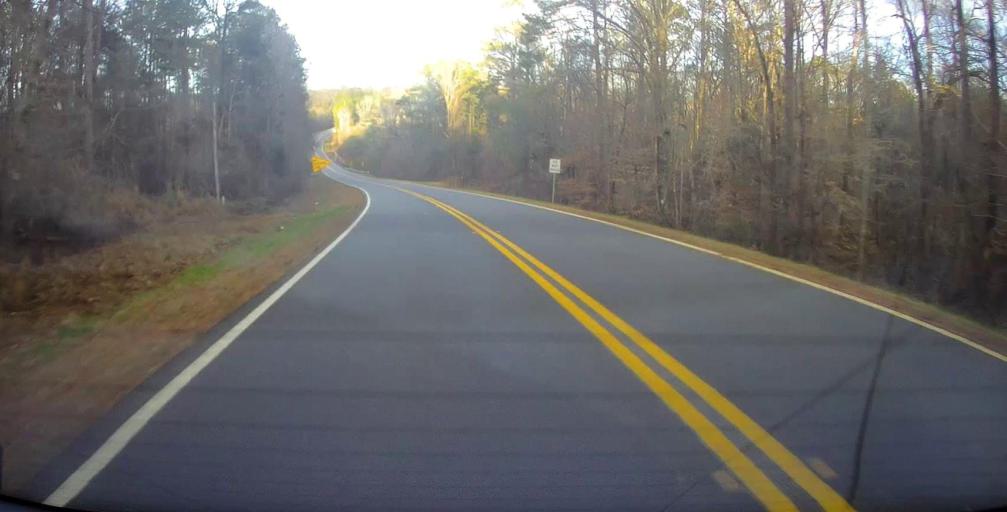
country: US
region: Georgia
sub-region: Talbot County
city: Sardis
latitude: 32.7586
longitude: -84.5665
